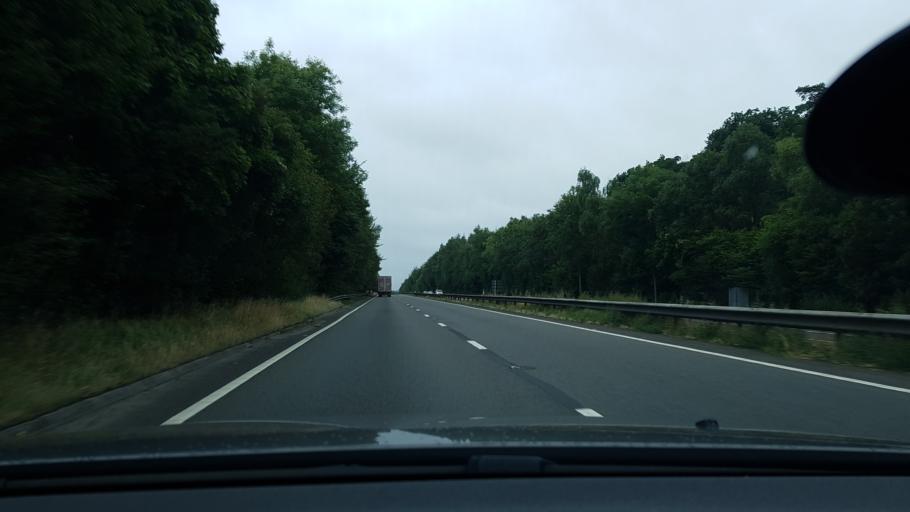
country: GB
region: England
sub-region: Hampshire
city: Highclere
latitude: 51.2722
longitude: -1.3433
